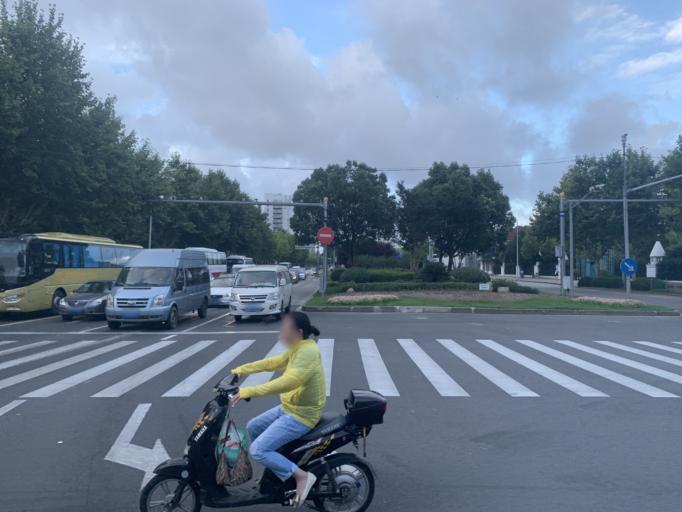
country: CN
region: Shanghai Shi
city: Pudong
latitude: 31.2480
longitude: 121.5607
